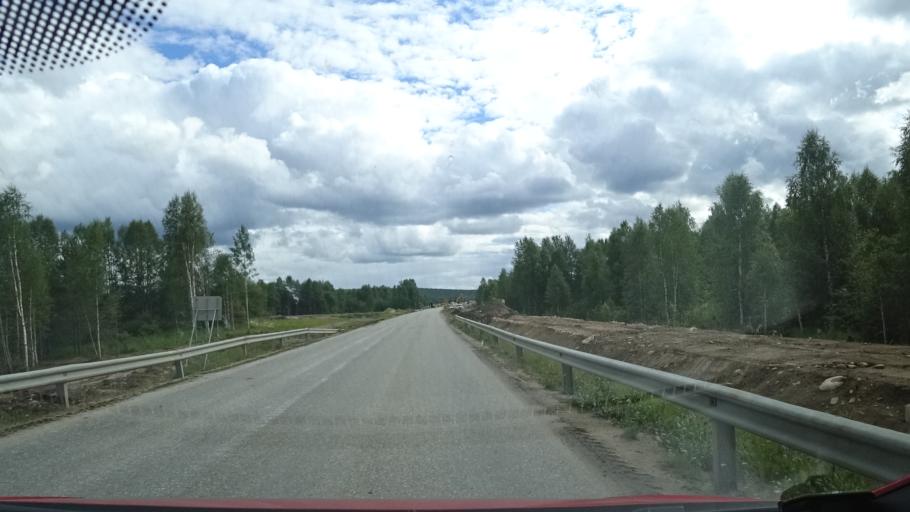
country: FI
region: Lapland
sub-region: Rovaniemi
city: Rovaniemi
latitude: 66.5267
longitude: 25.7423
